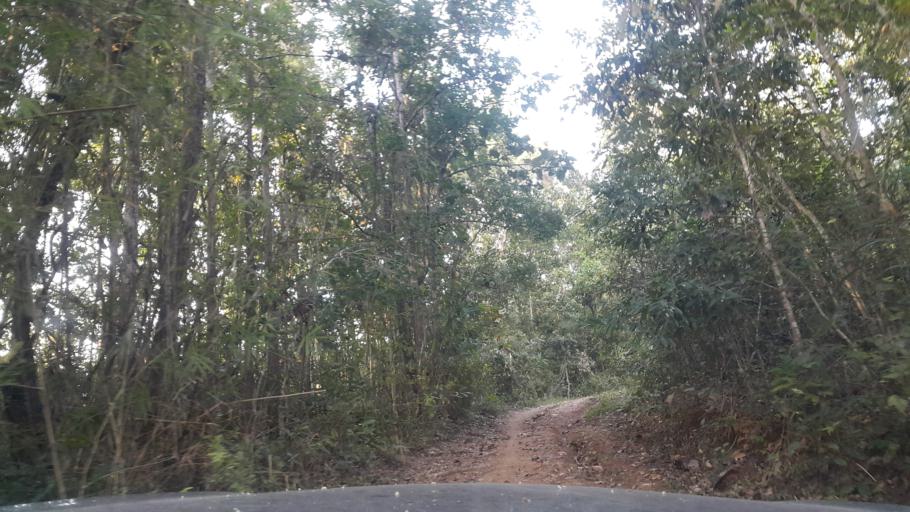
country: TH
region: Chiang Mai
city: Samoeng
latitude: 18.9049
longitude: 98.8609
